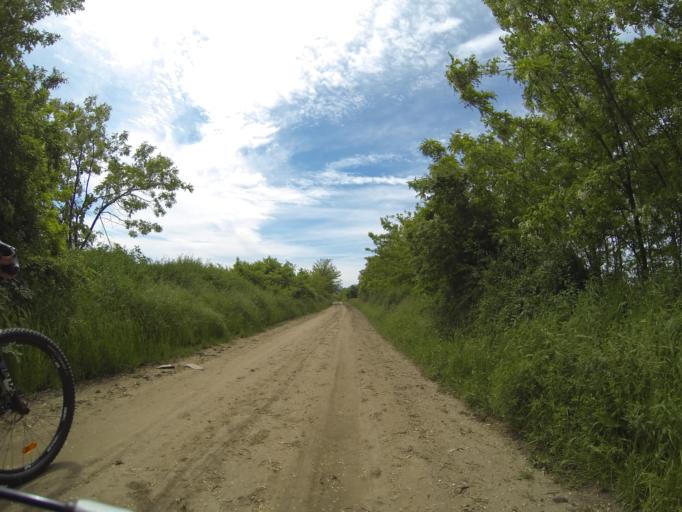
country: RO
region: Dolj
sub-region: Comuna Leu
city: Leu
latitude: 44.1992
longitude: 24.0041
